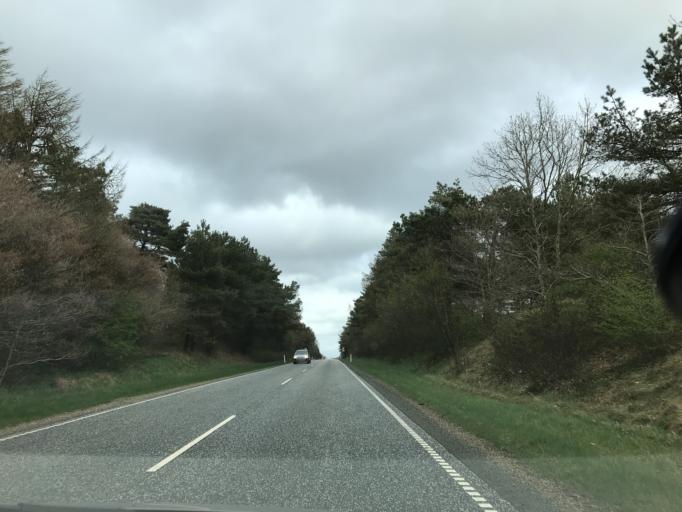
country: DK
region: Central Jutland
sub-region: Skive Kommune
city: Skive
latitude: 56.5223
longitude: 8.9633
